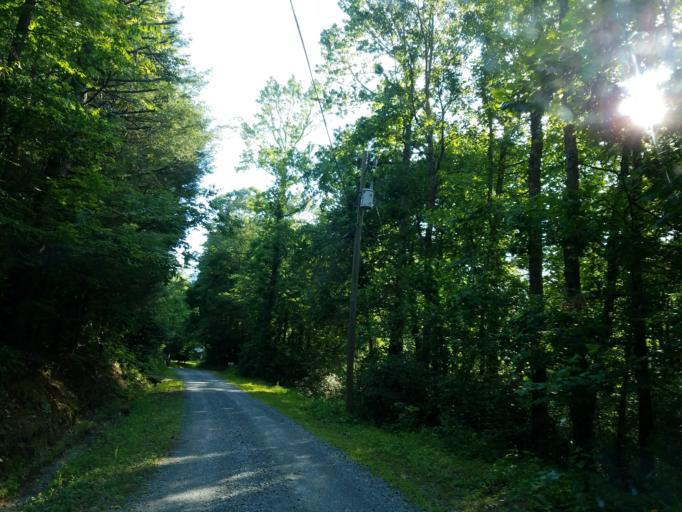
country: US
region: Georgia
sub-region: Dawson County
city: Dawsonville
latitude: 34.6273
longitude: -84.2416
